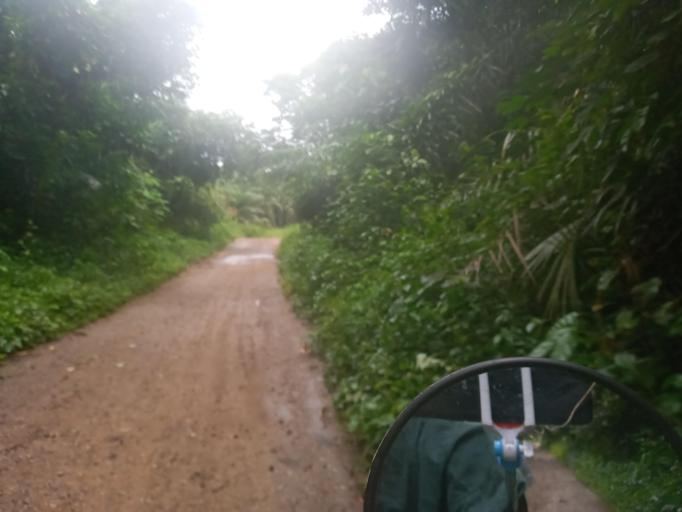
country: SL
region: Northern Province
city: Bumbuna
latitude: 8.9416
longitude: -11.7497
